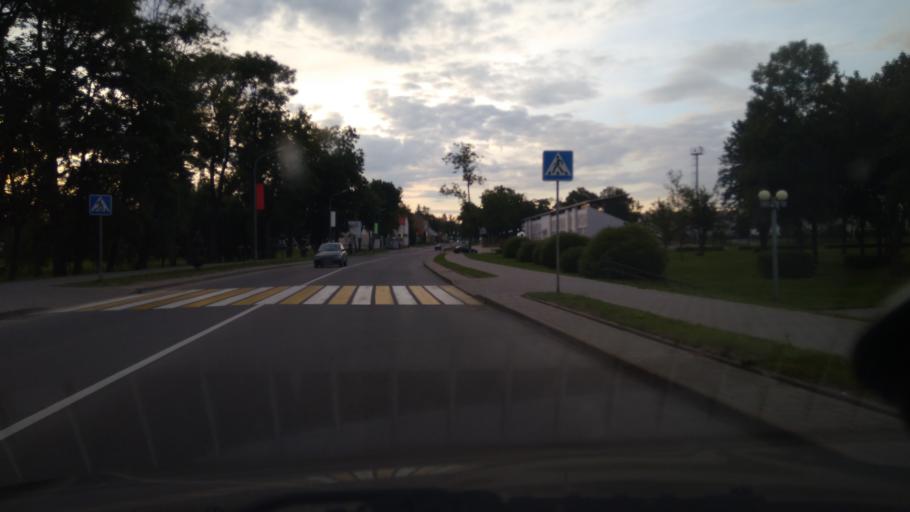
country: BY
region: Grodnenskaya
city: Shchuchin
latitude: 53.6083
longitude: 24.7392
